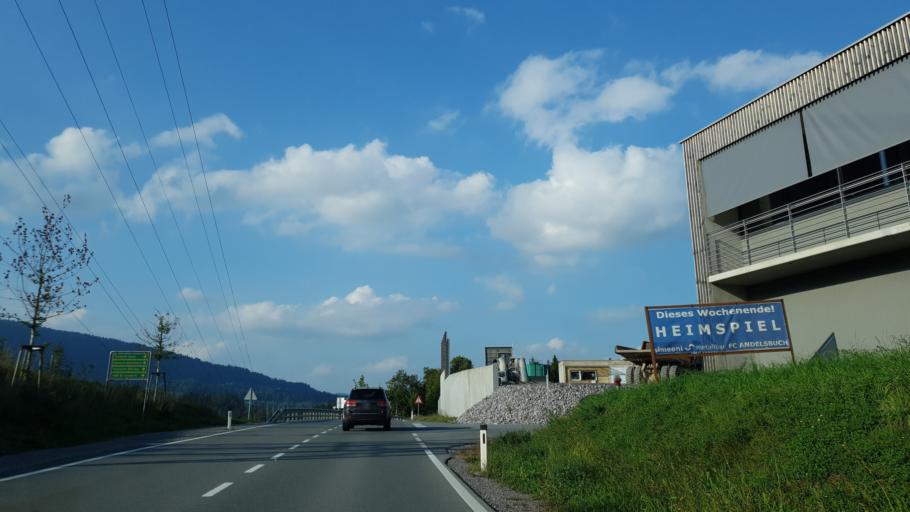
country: AT
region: Vorarlberg
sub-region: Politischer Bezirk Bregenz
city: Andelsbuch
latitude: 47.4034
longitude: 9.8787
